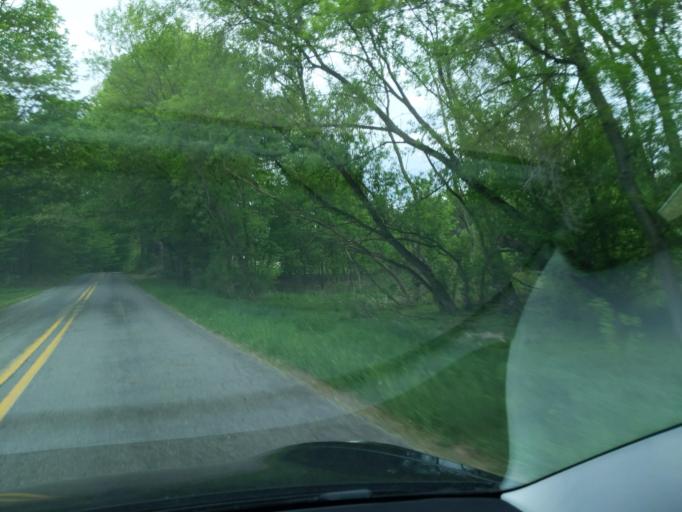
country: US
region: Michigan
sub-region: Ingham County
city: Stockbridge
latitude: 42.5125
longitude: -84.2771
